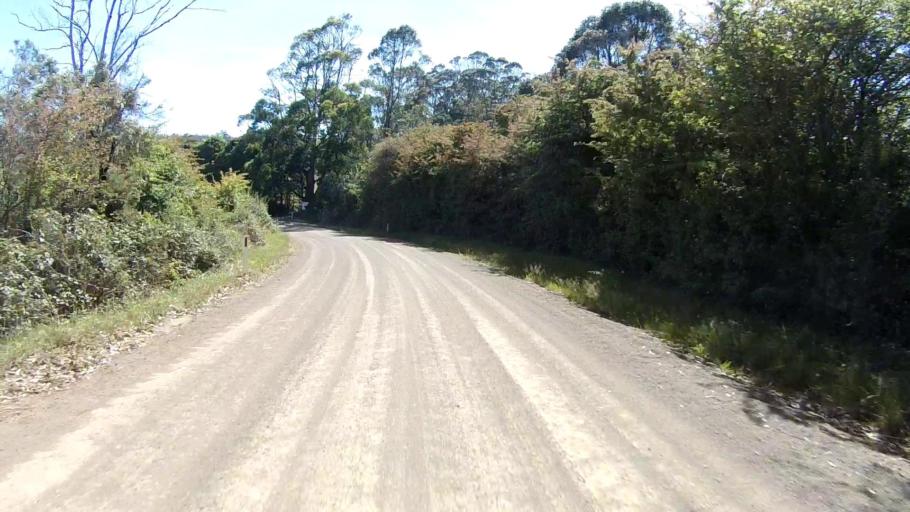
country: AU
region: Tasmania
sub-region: Sorell
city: Sorell
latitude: -42.7175
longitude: 147.7509
